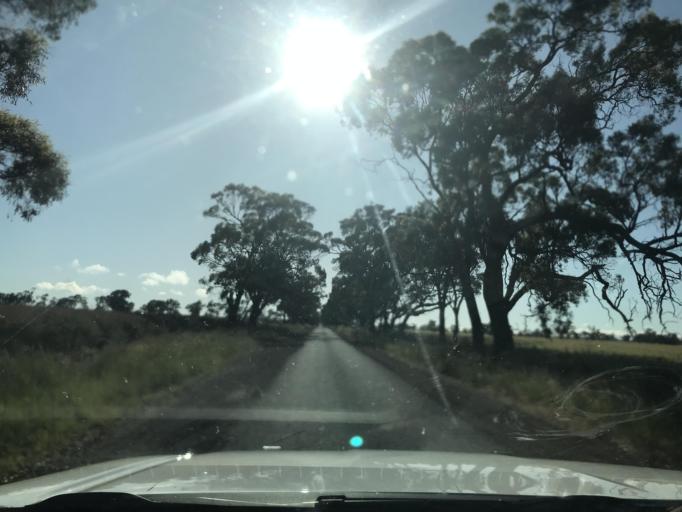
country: AU
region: Victoria
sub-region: Horsham
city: Horsham
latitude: -36.6909
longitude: 141.5330
